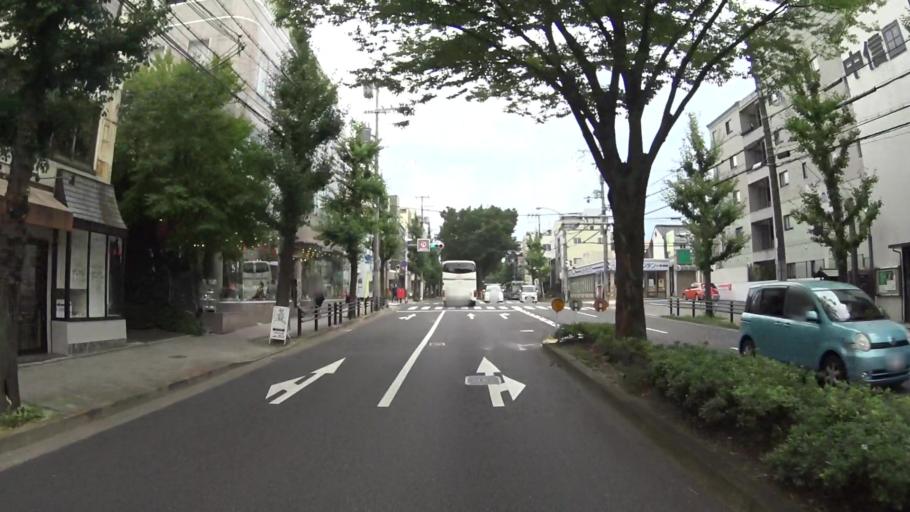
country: JP
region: Kyoto
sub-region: Kyoto-shi
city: Kamigyo-ku
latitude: 35.0290
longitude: 135.7914
